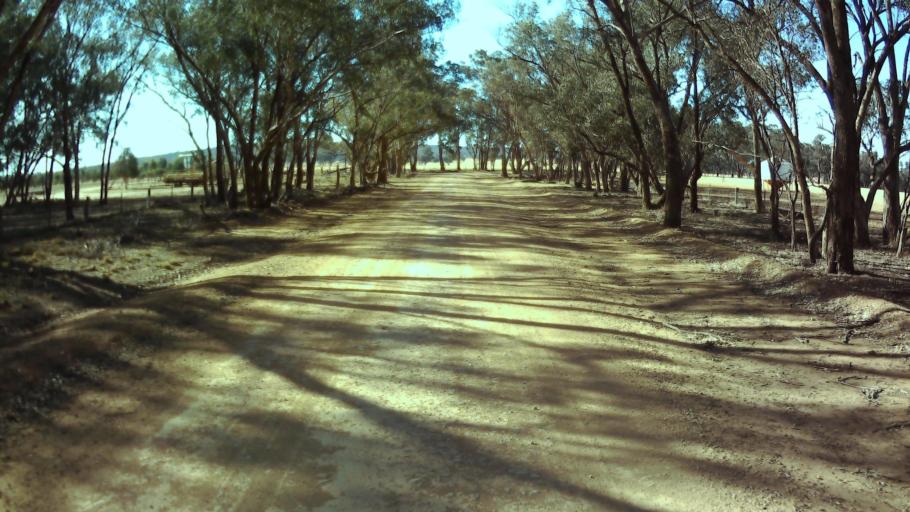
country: AU
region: New South Wales
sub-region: Weddin
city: Grenfell
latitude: -33.8366
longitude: 147.8735
